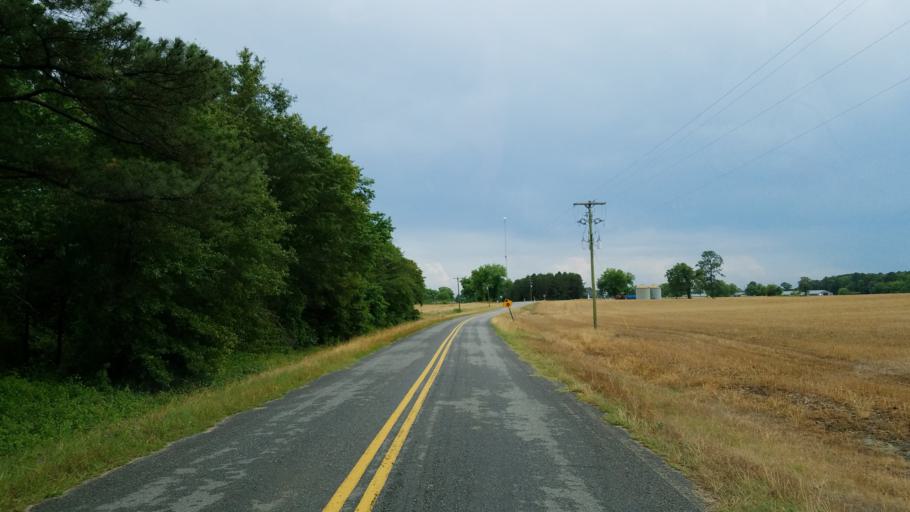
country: US
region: Georgia
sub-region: Dooly County
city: Unadilla
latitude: 32.2494
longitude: -83.7973
